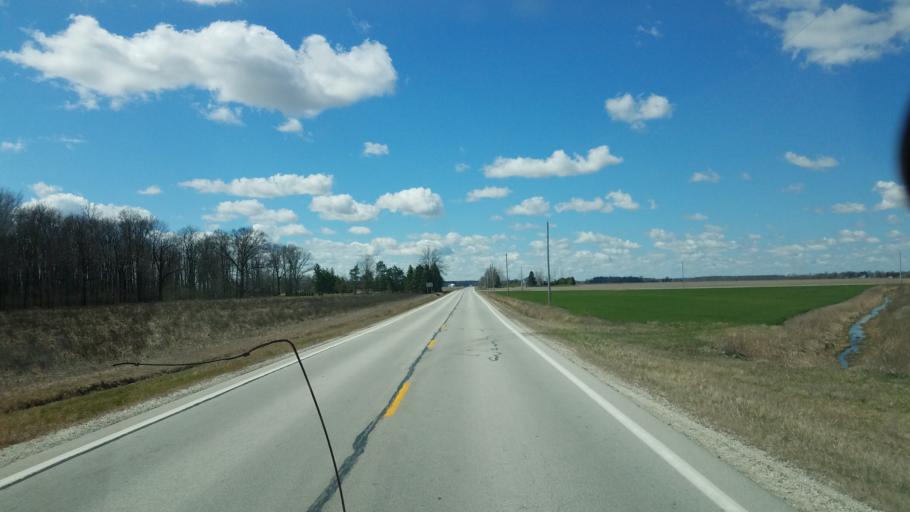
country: US
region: Ohio
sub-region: Seneca County
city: Fostoria
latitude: 41.2178
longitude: -83.2909
